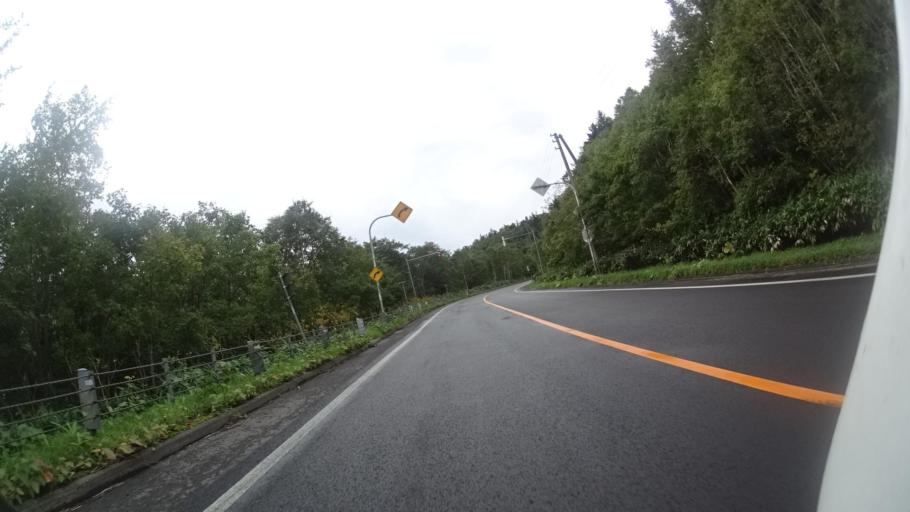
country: JP
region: Hokkaido
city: Shibetsu
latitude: 43.7756
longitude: 144.7954
